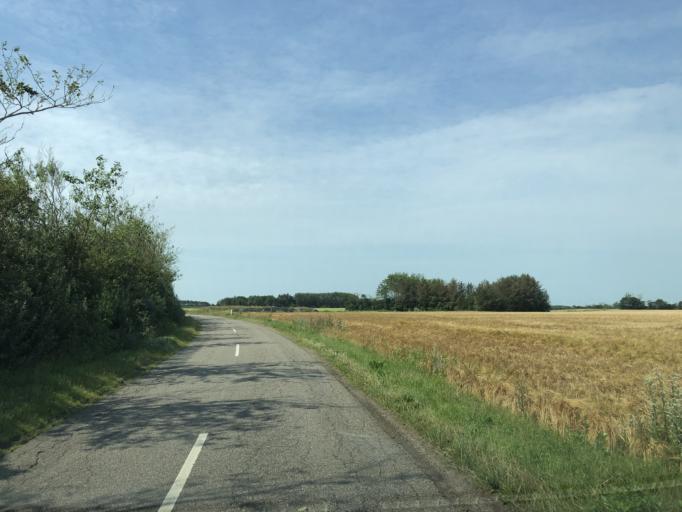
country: DK
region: Central Jutland
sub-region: Lemvig Kommune
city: Lemvig
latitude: 56.4364
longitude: 8.2785
